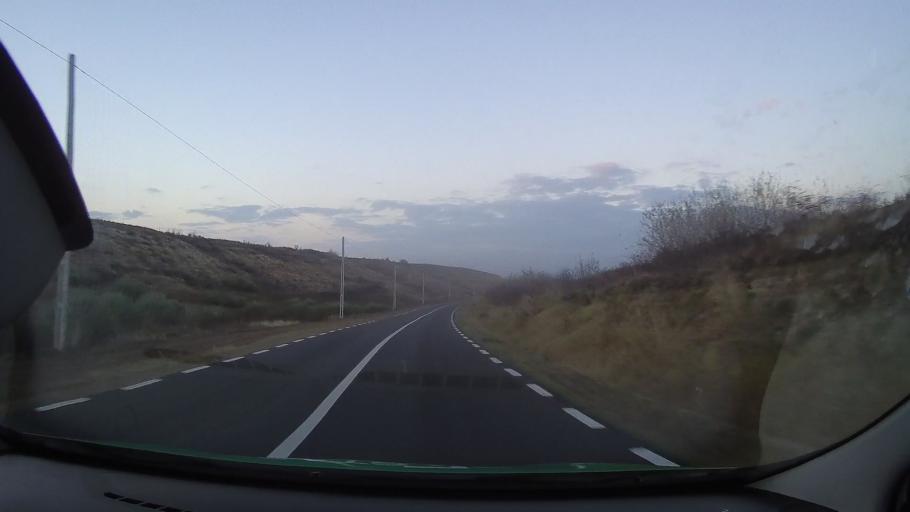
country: RO
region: Constanta
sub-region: Comuna Oltina
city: Oltina
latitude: 44.1376
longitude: 27.6657
